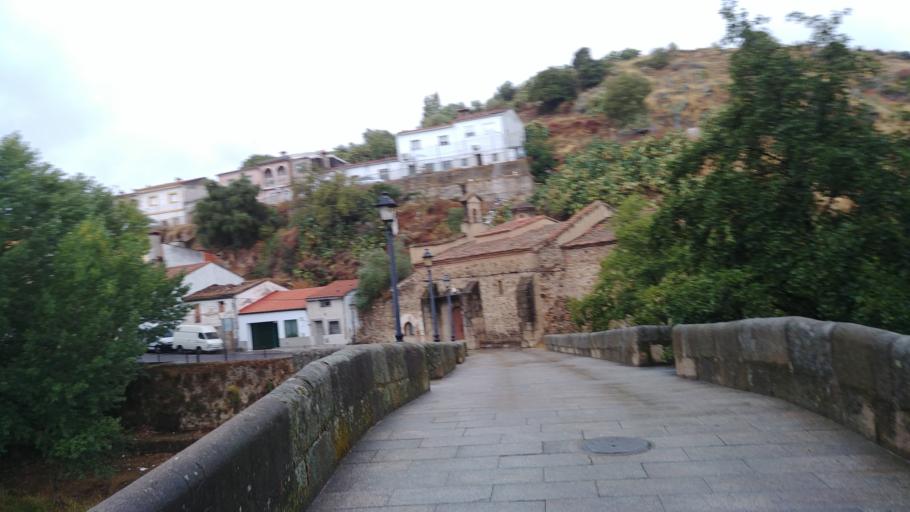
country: ES
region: Extremadura
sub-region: Provincia de Caceres
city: Plasencia
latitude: 40.0299
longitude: -6.0962
